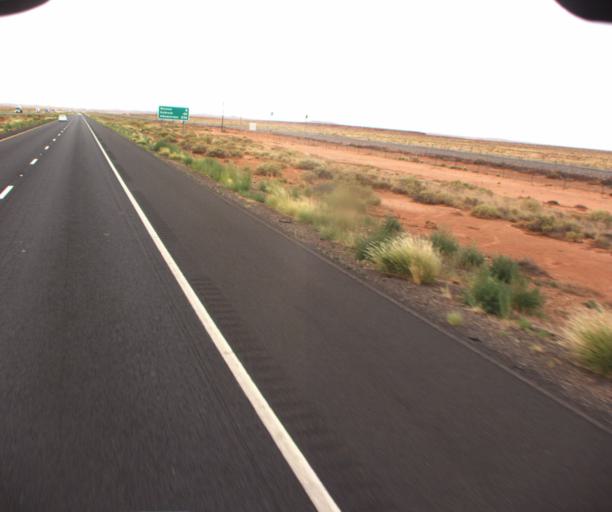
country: US
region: Arizona
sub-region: Coconino County
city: LeChee
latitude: 35.0631
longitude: -110.8211
